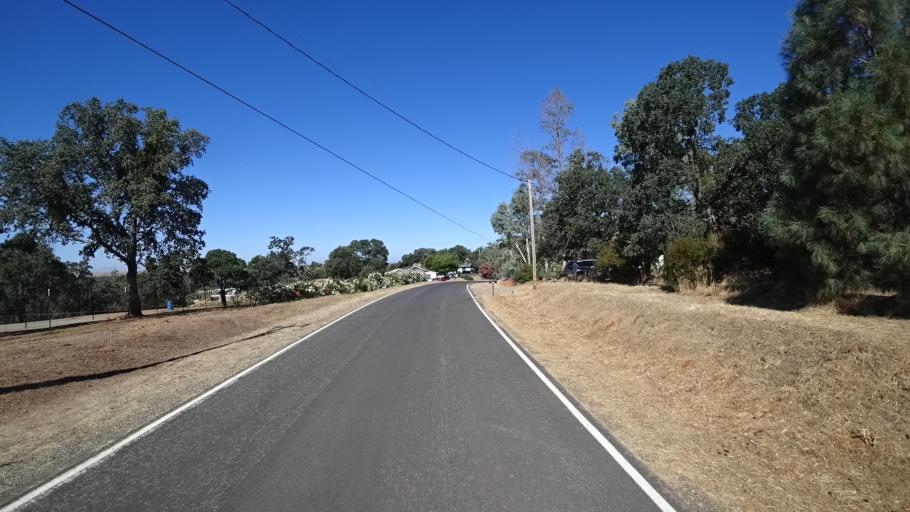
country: US
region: California
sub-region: Calaveras County
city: Rancho Calaveras
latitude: 38.1008
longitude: -120.8641
